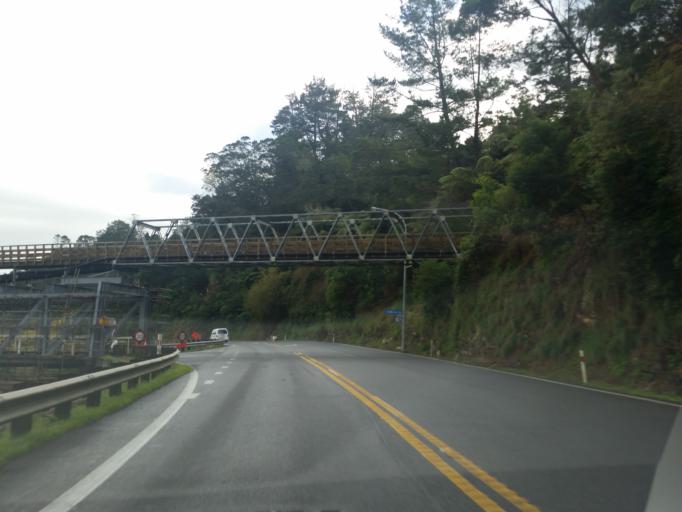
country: NZ
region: Waikato
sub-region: Hauraki District
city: Paeroa
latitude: -37.4187
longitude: 175.7188
